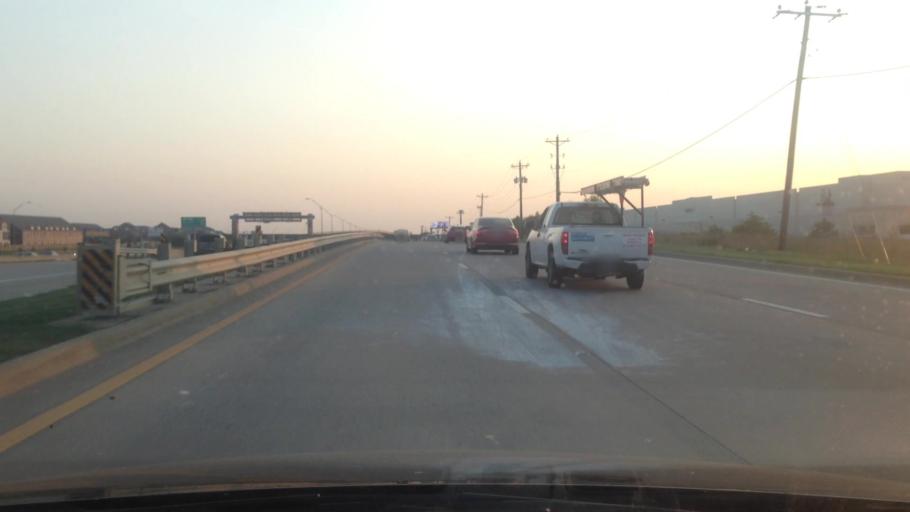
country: US
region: Texas
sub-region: Denton County
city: The Colony
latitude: 33.0571
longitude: -96.9091
